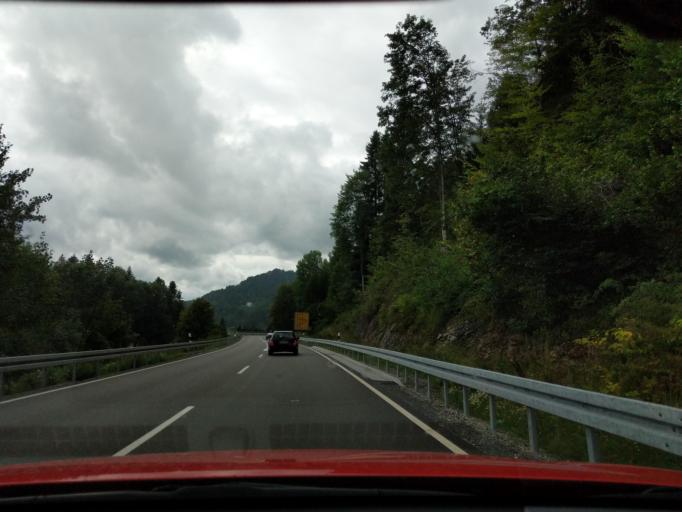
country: DE
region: Bavaria
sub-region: Swabia
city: Oberstaufen
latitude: 47.5492
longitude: 10.0312
